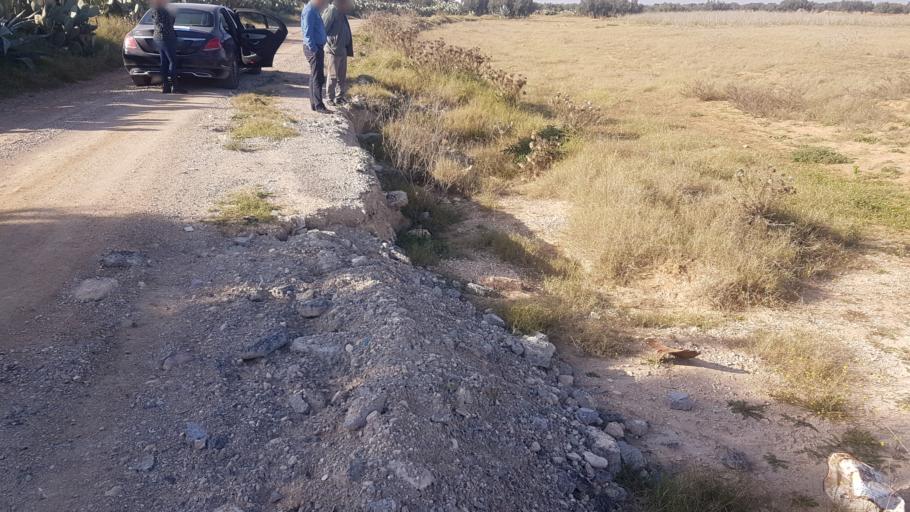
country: TN
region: Al Munastir
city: Bani Hassan
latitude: 35.4665
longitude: 10.6975
